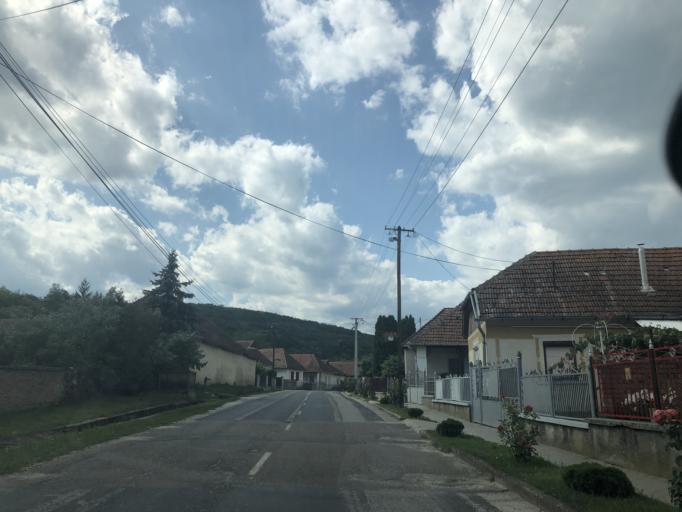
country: HU
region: Borsod-Abauj-Zemplen
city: Szendro
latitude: 48.4381
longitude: 20.7968
